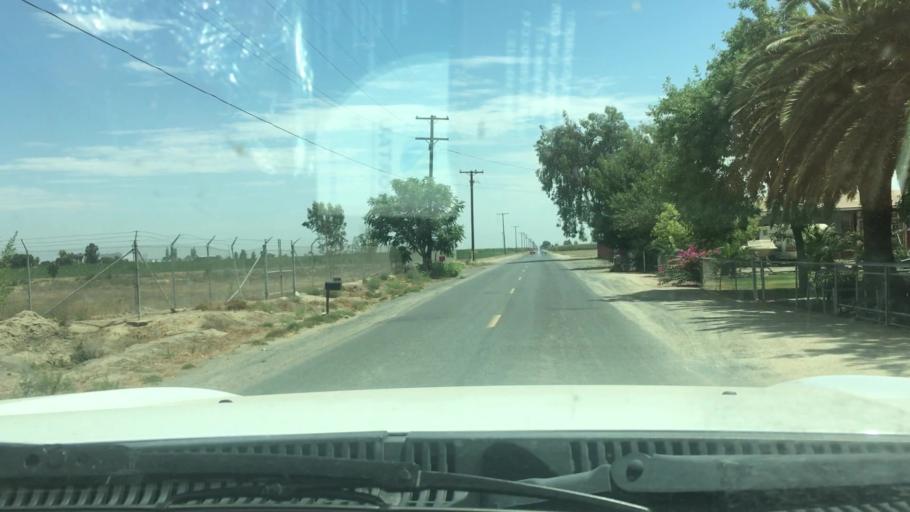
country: US
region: California
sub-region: Tulare County
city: Tipton
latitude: 36.0630
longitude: -119.3220
